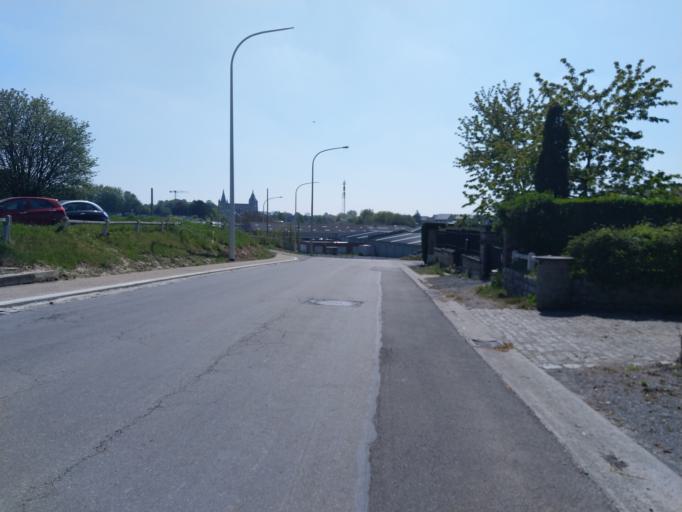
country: BE
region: Wallonia
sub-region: Province du Hainaut
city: Soignies
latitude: 50.5873
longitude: 4.0703
